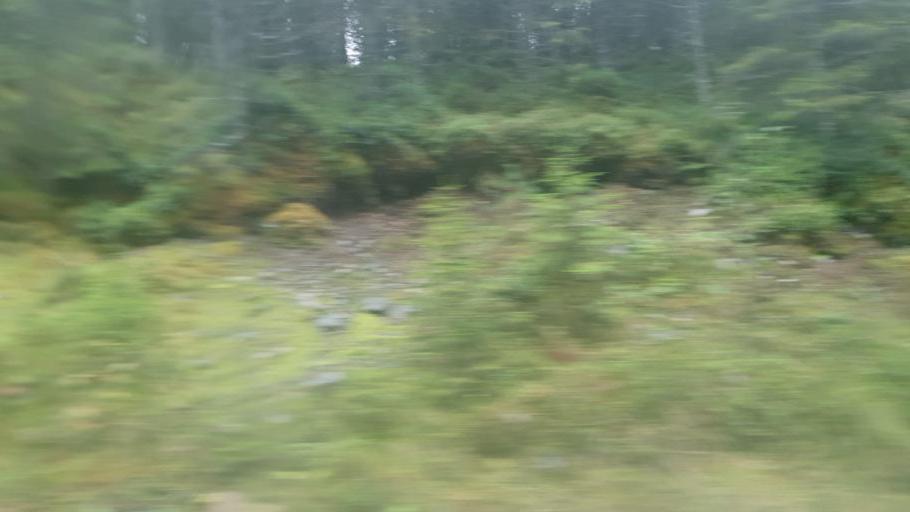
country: NO
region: Nord-Trondelag
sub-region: Levanger
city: Skogn
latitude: 63.6168
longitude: 11.2205
